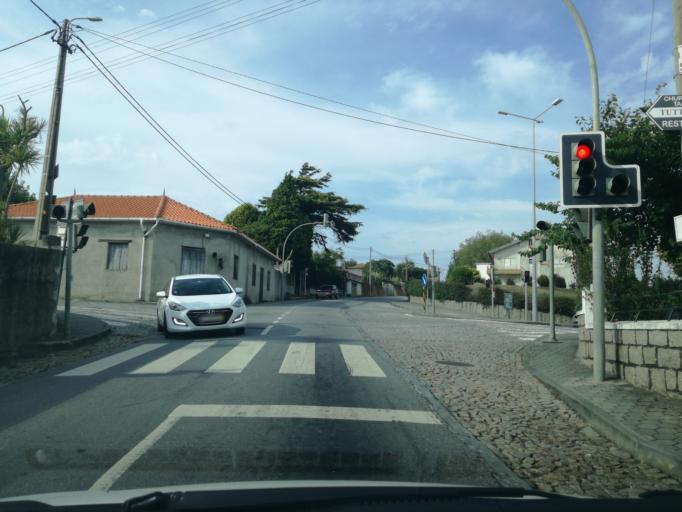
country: PT
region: Porto
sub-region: Vila Nova de Gaia
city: Sao Felix da Marinha
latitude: 41.0341
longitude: -8.6303
